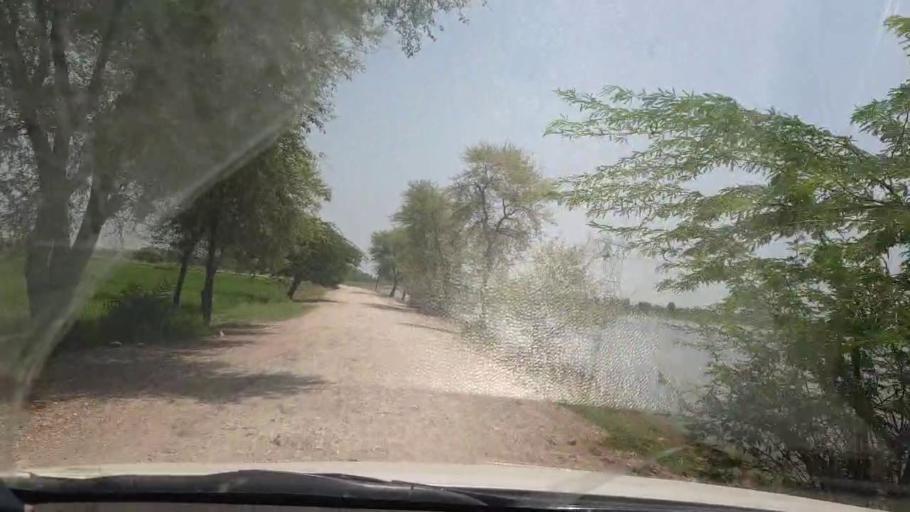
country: PK
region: Sindh
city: Shikarpur
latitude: 27.9171
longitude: 68.6853
